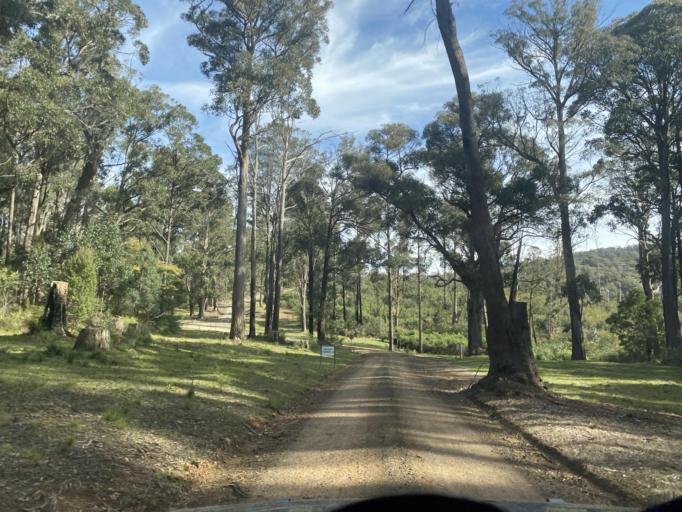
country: AU
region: Victoria
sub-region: Mansfield
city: Mansfield
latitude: -36.8473
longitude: 146.1810
